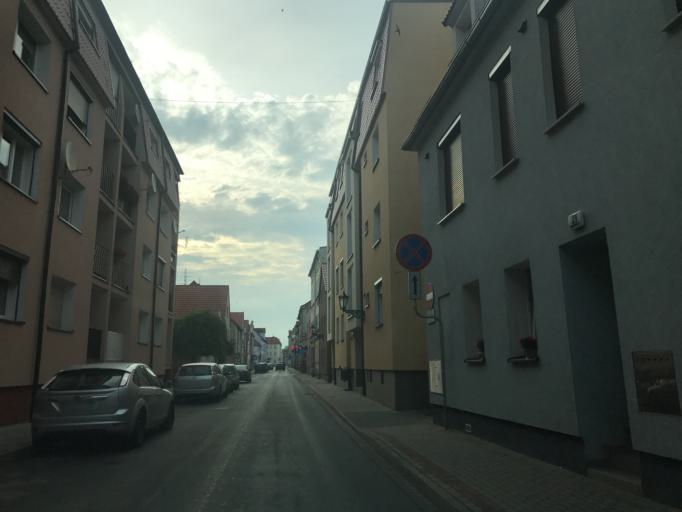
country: PL
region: Greater Poland Voivodeship
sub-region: Powiat rawicki
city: Rawicz
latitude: 51.6088
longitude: 16.8540
